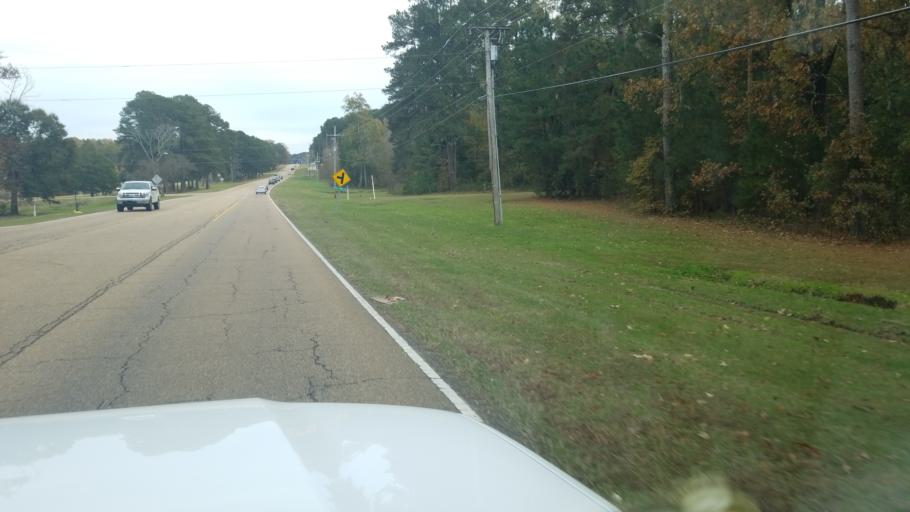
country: US
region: Mississippi
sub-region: Madison County
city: Ridgeland
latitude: 32.3783
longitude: -90.0311
